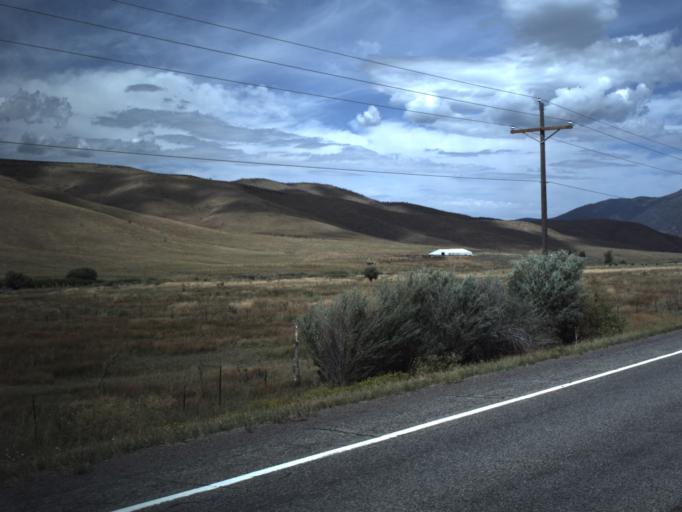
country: US
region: Utah
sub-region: Sanpete County
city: Fairview
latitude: 39.8169
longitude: -111.5071
